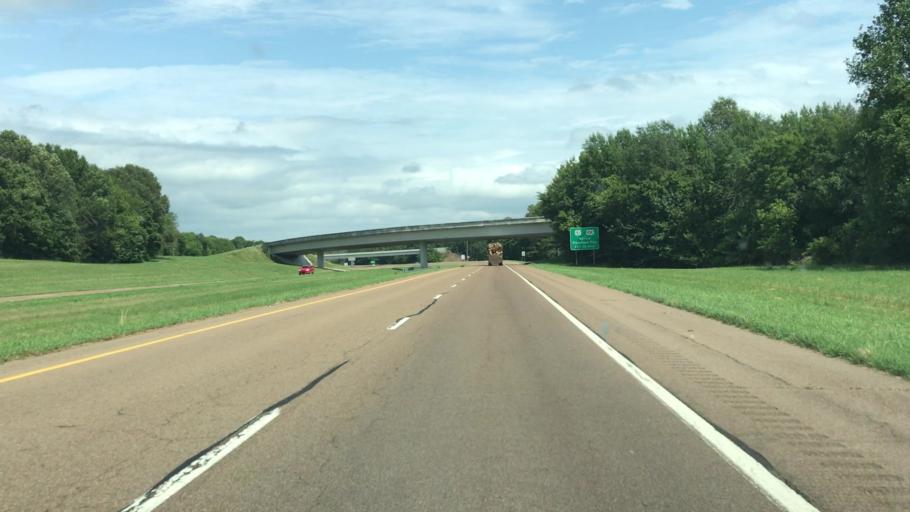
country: US
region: Tennessee
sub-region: Obion County
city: South Fulton
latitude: 36.4948
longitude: -88.9108
